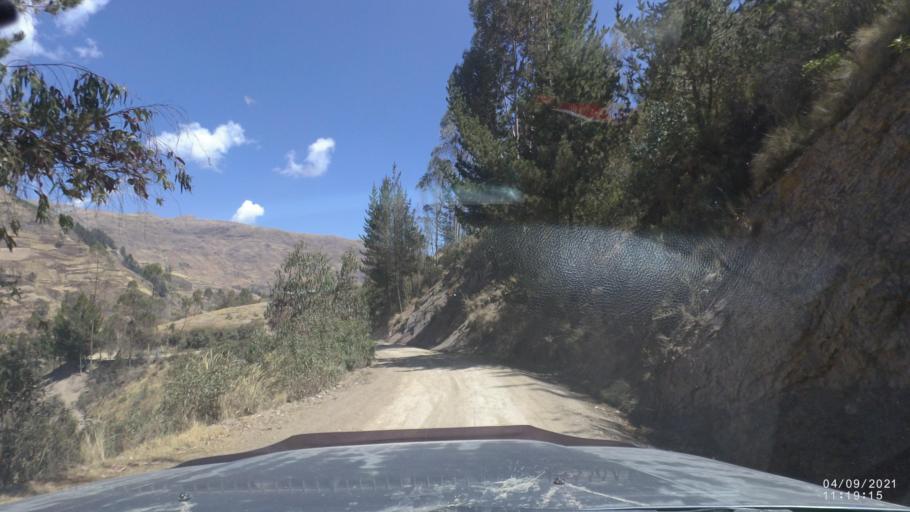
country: BO
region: Cochabamba
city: Sipe Sipe
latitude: -17.2660
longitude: -66.4957
